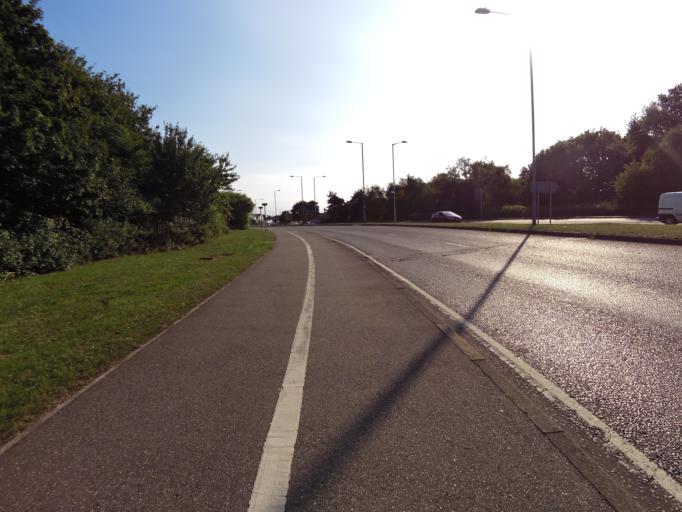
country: GB
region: England
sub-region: Essex
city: Chelmsford
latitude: 51.7470
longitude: 0.5026
